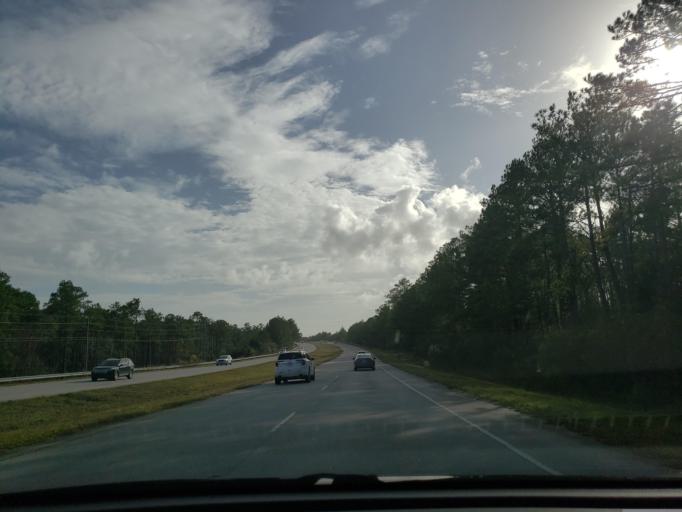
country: US
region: North Carolina
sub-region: Onslow County
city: Sneads Ferry
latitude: 34.6211
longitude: -77.4837
